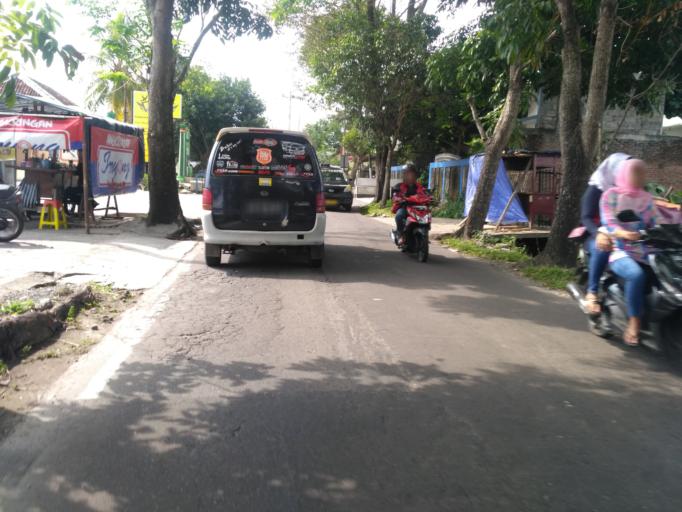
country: ID
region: Daerah Istimewa Yogyakarta
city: Melati
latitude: -7.7302
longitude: 110.3552
